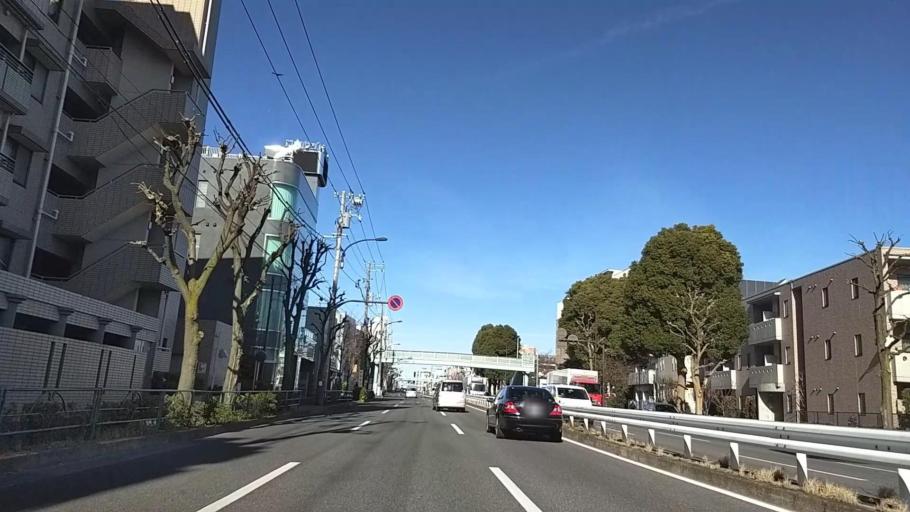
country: JP
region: Kanagawa
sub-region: Kawasaki-shi
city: Kawasaki
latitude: 35.5944
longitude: 139.6740
